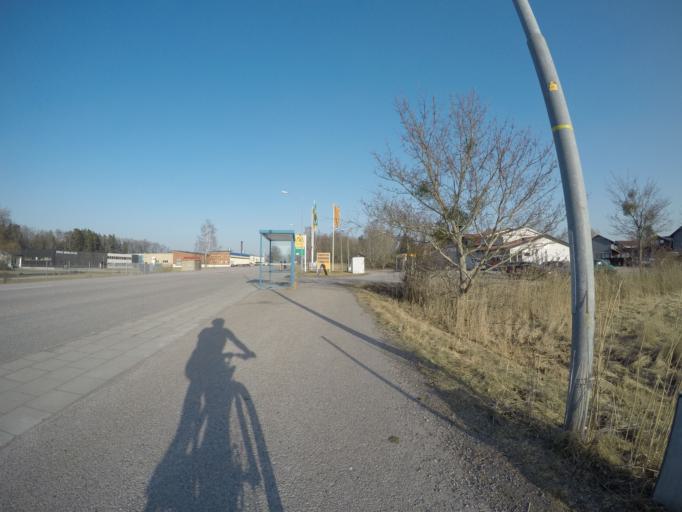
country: SE
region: Vaestmanland
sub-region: Kungsors Kommun
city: Kungsoer
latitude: 59.4255
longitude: 16.1186
